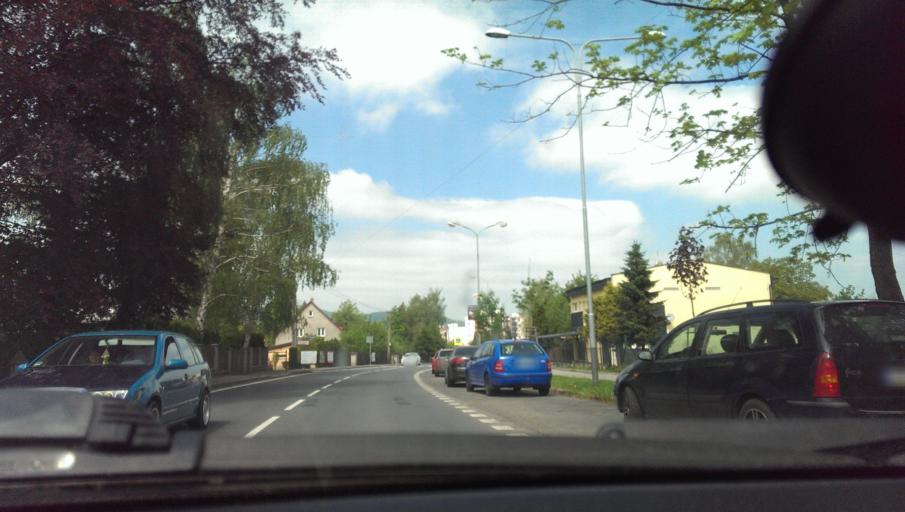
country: CZ
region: Moravskoslezsky
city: Frenstat pod Radhostem
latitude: 49.5465
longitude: 18.2093
